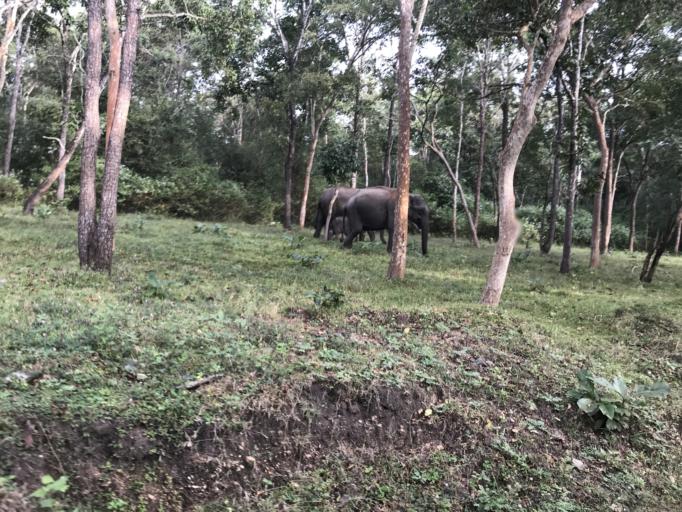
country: IN
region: Karnataka
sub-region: Mysore
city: Heggadadevankote
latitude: 12.0005
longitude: 76.2219
